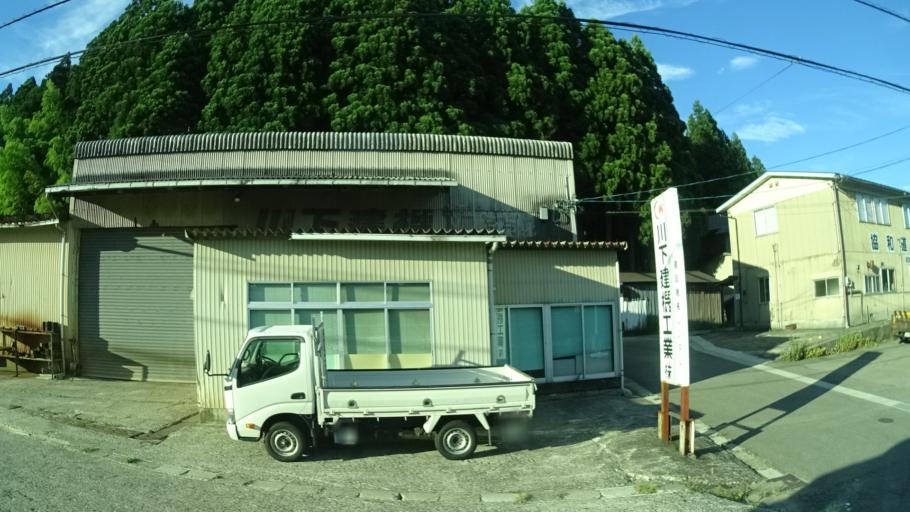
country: JP
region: Ishikawa
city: Nanao
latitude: 37.2453
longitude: 136.8969
